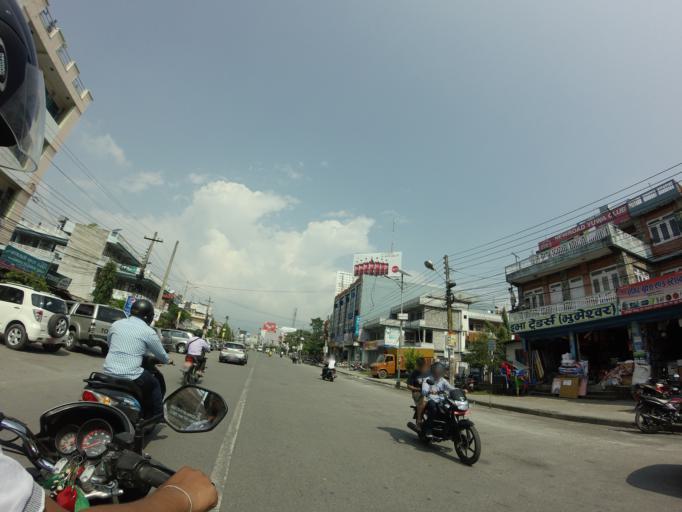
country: NP
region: Western Region
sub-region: Gandaki Zone
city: Pokhara
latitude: 28.2117
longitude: 83.9848
